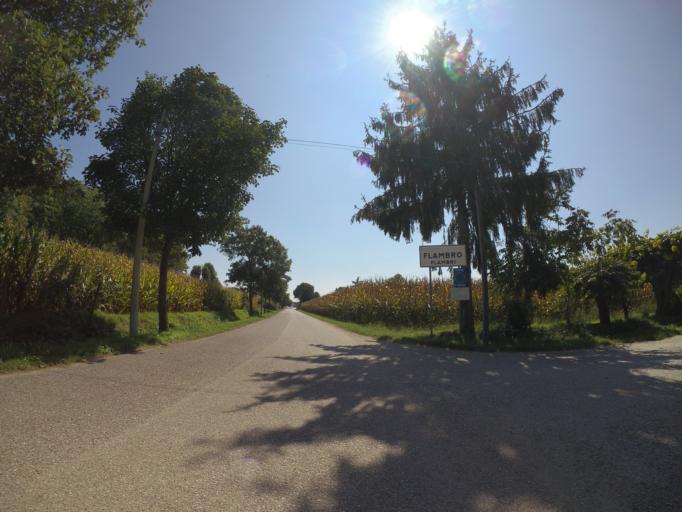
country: IT
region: Friuli Venezia Giulia
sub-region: Provincia di Udine
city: Talmassons
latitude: 45.9391
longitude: 13.0900
